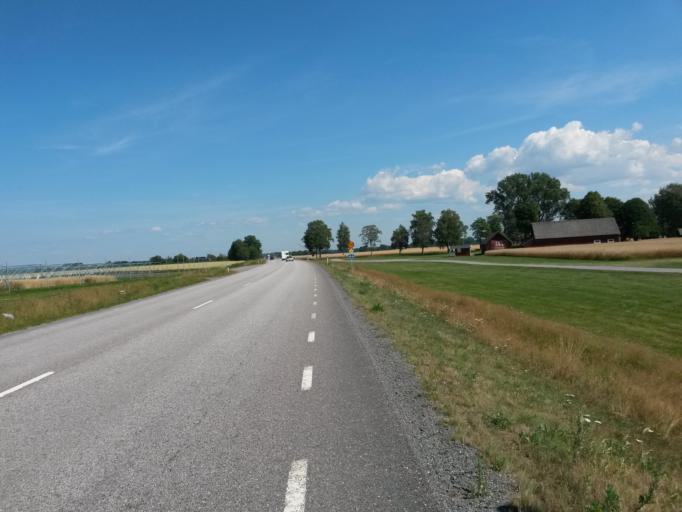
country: SE
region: Vaestra Goetaland
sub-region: Lidkopings Kommun
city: Lidkoping
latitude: 58.4800
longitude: 13.0909
